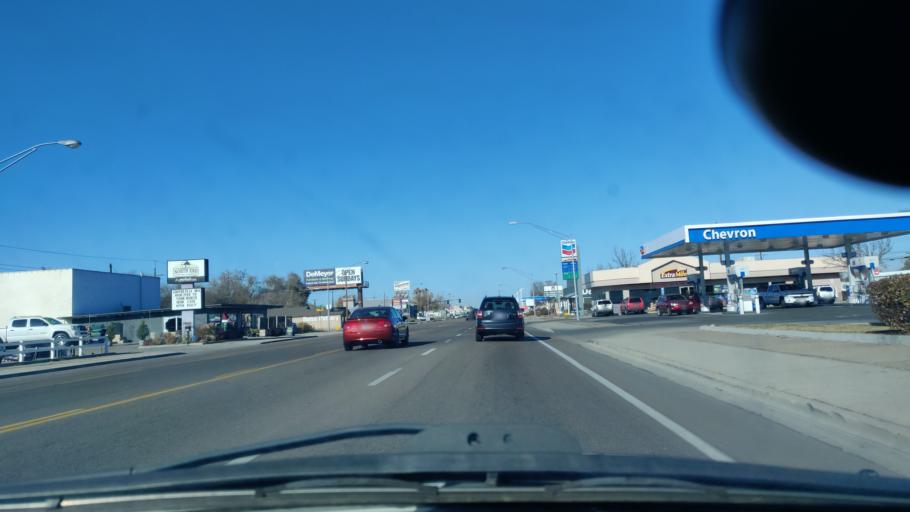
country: US
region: Idaho
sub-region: Ada County
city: Garden City
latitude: 43.6257
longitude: -116.2434
